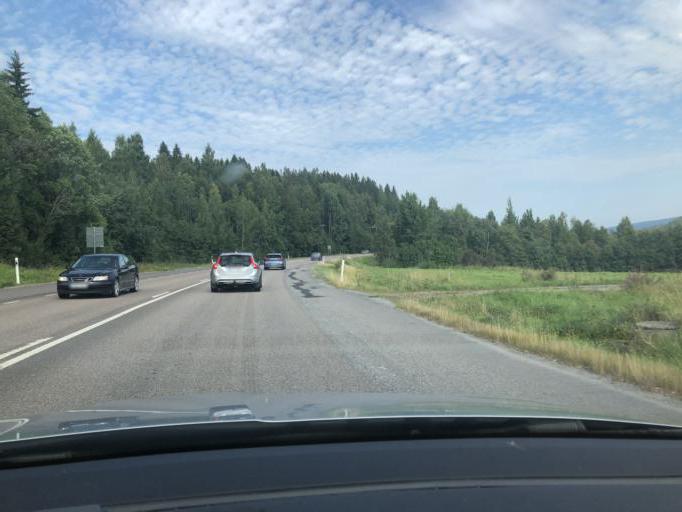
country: SE
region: Vaesternorrland
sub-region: Kramfors Kommun
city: Kramfors
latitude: 62.8826
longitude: 17.8497
